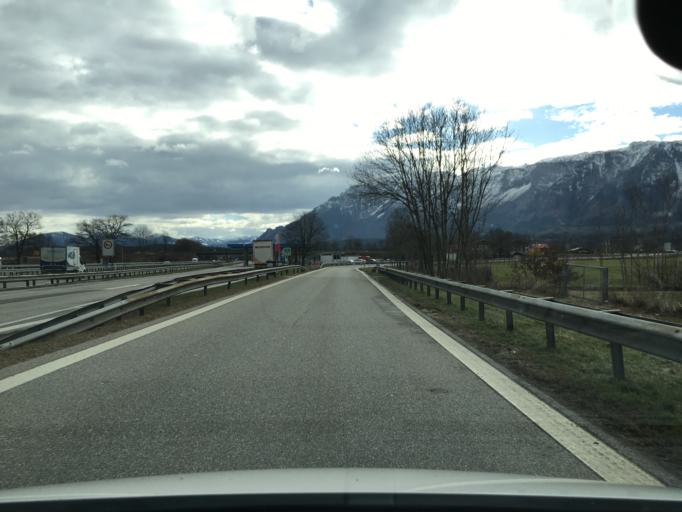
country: DE
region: Bavaria
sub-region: Upper Bavaria
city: Piding
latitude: 47.7675
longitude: 12.9006
